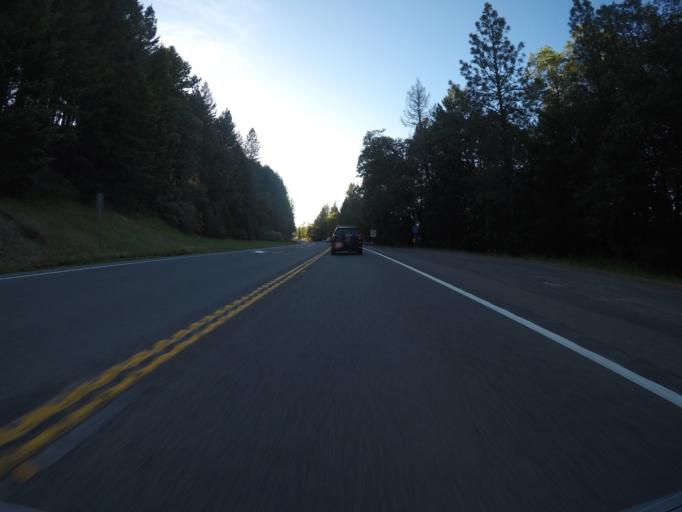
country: US
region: California
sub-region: Mendocino County
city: Laytonville
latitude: 39.7106
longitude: -123.4917
